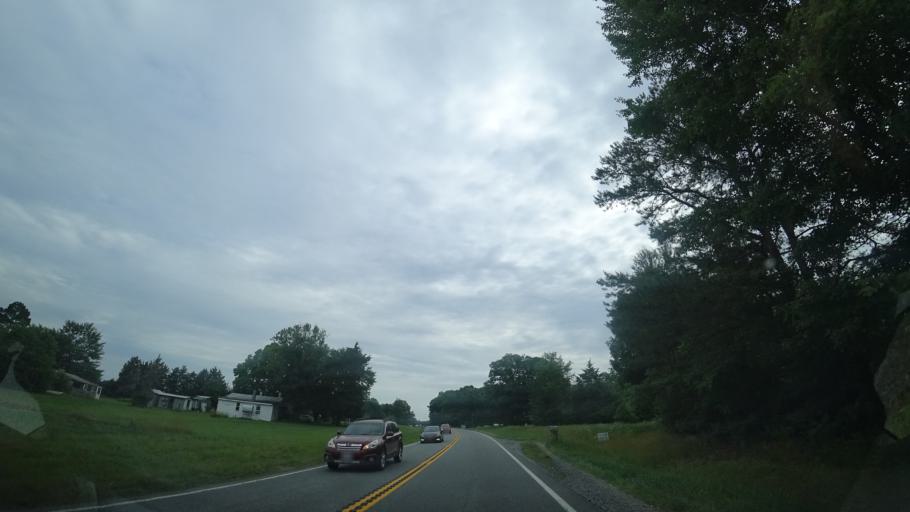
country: US
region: Virginia
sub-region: Spotsylvania County
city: Spotsylvania Courthouse
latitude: 38.1272
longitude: -77.7364
